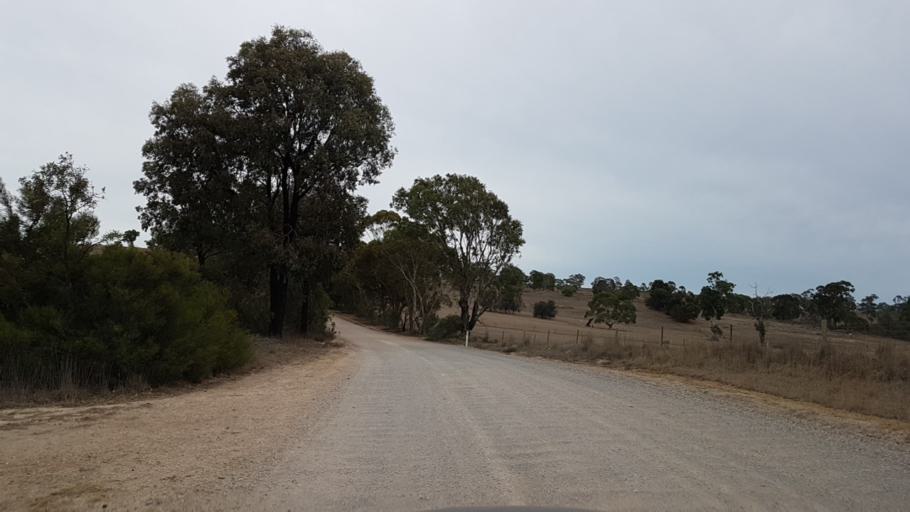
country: AU
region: South Australia
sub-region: Mount Barker
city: Nairne
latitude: -34.9978
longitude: 138.9890
